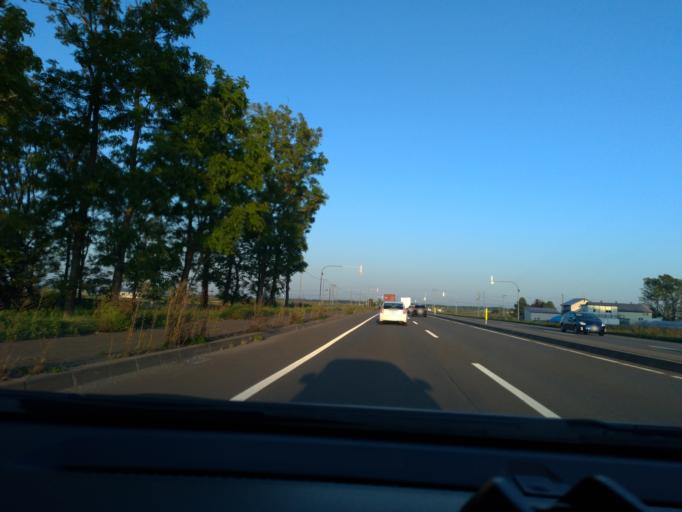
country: JP
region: Hokkaido
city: Tobetsu
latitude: 43.1785
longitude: 141.4531
